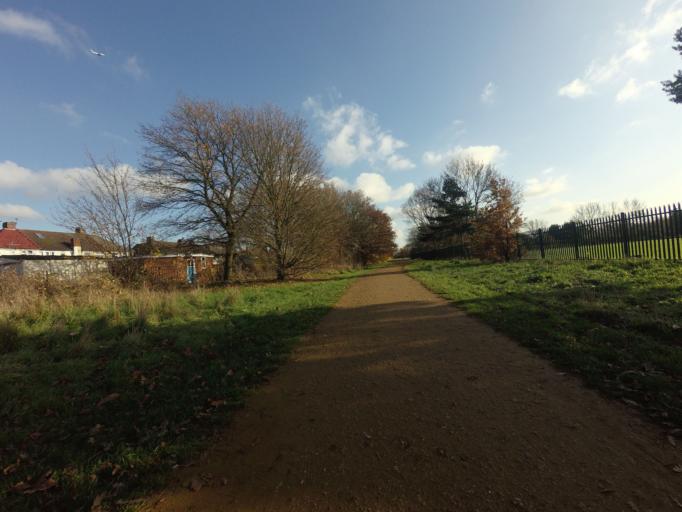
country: GB
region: England
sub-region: Greater London
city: Feltham
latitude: 51.4435
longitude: -0.3970
